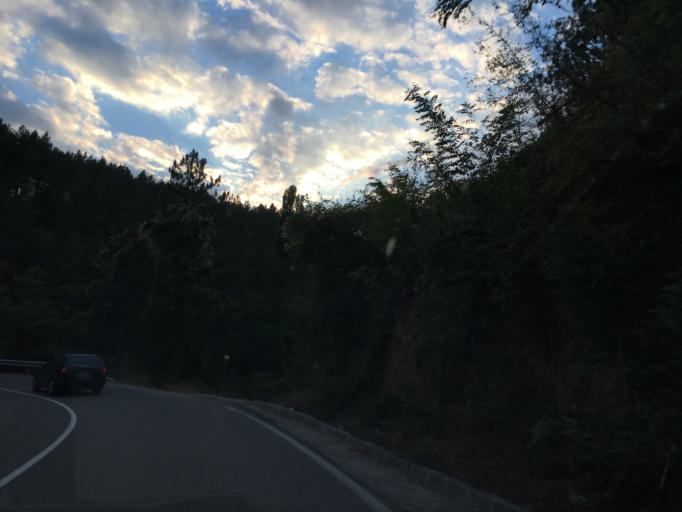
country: BG
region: Sofiya
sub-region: Obshtina Svoge
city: Svoge
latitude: 42.8354
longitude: 23.3531
